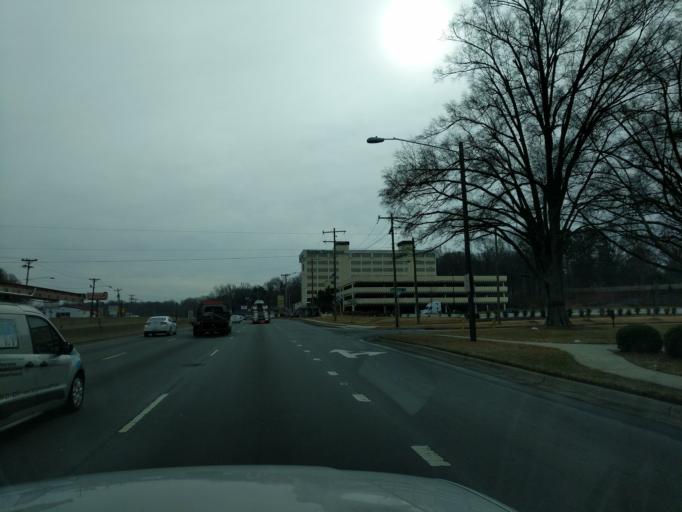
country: US
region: North Carolina
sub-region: Mecklenburg County
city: Charlotte
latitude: 35.2053
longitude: -80.7943
